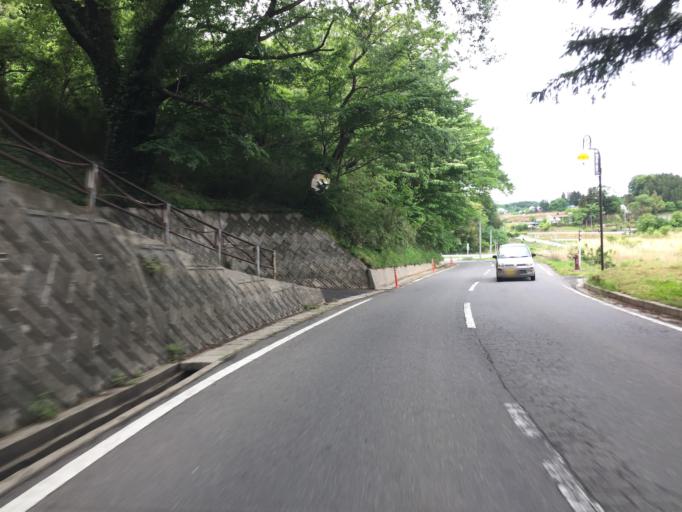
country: JP
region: Fukushima
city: Miharu
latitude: 37.4916
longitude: 140.4642
